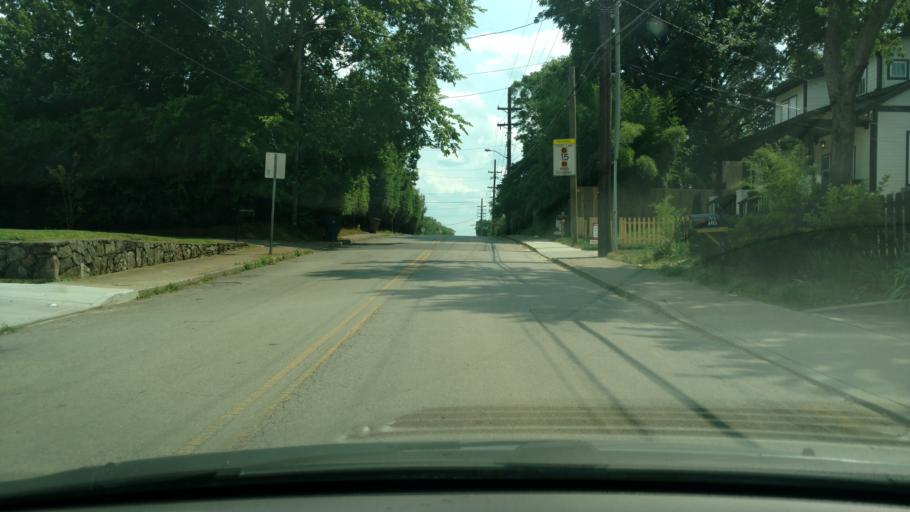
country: US
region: Tennessee
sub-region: Davidson County
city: Nashville
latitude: 36.1902
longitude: -86.7336
